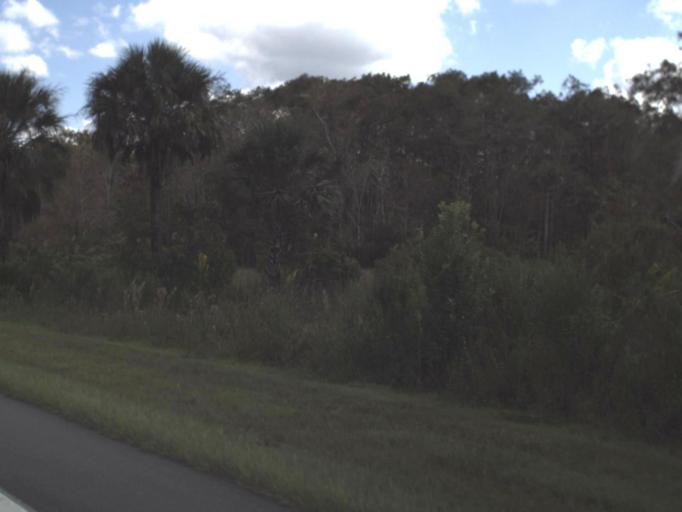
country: US
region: Florida
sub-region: Collier County
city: Marco
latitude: 25.8731
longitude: -81.1932
